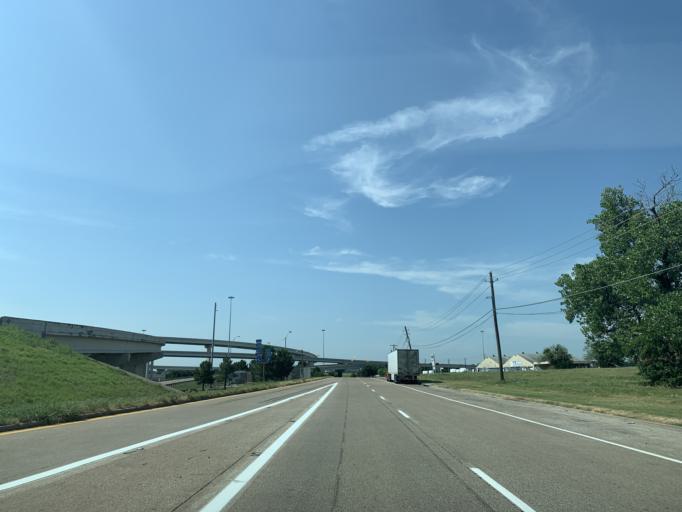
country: US
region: Texas
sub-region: Tarrant County
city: Edgecliff Village
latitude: 32.6708
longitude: -97.3213
